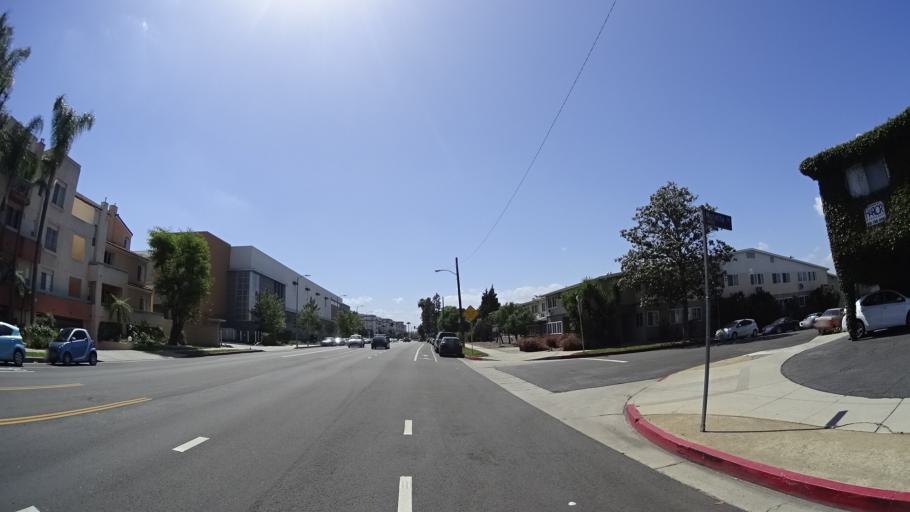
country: US
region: California
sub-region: Los Angeles County
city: Sherman Oaks
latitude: 34.1504
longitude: -118.4382
